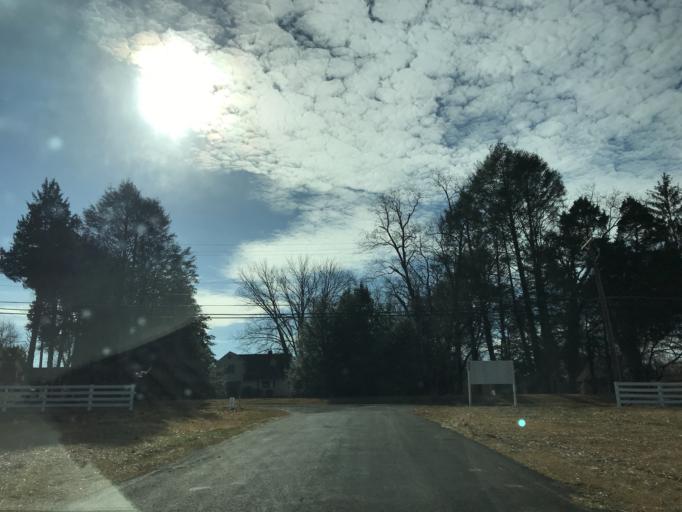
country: US
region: Maryland
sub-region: Baltimore County
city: Kingsville
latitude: 39.4518
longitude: -76.4082
